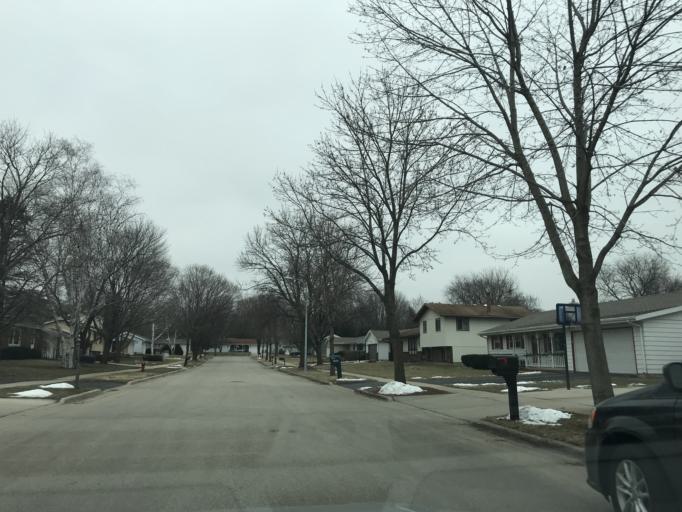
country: US
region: Wisconsin
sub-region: Dane County
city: Monona
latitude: 43.1015
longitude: -89.3036
